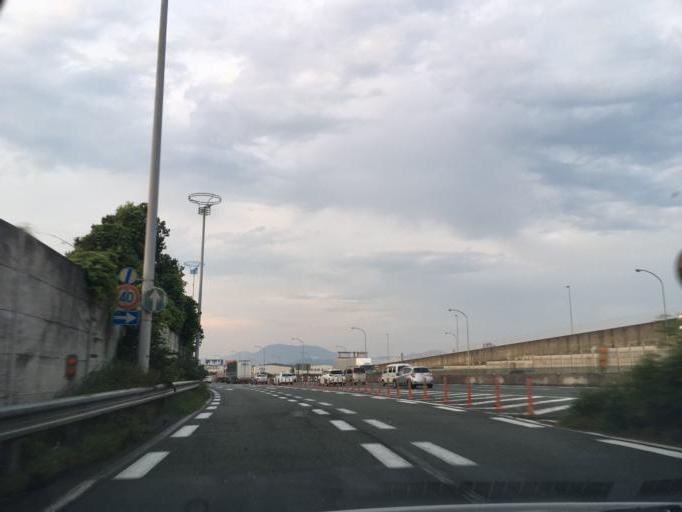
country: JP
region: Saga Prefecture
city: Tosu
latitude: 33.3991
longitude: 130.5381
